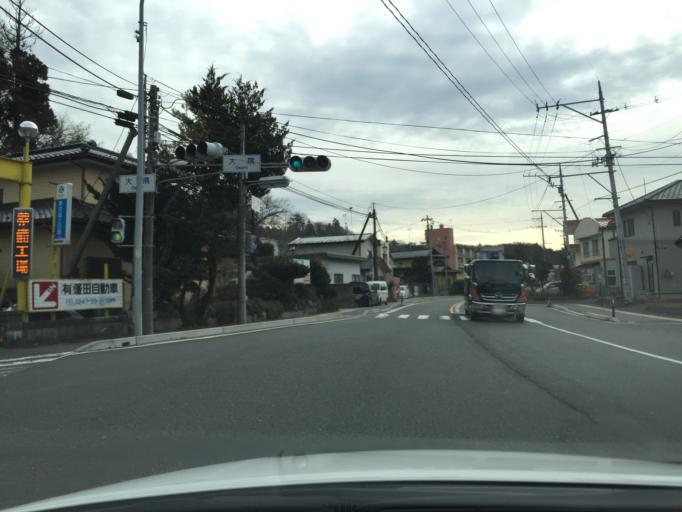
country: JP
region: Fukushima
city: Ishikawa
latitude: 37.2448
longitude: 140.5685
